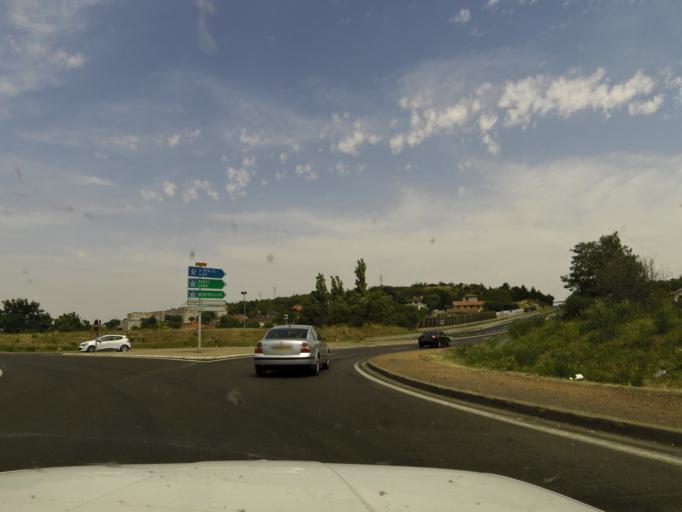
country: FR
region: Auvergne
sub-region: Departement du Puy-de-Dome
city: Aubiere
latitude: 45.7421
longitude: 3.1046
